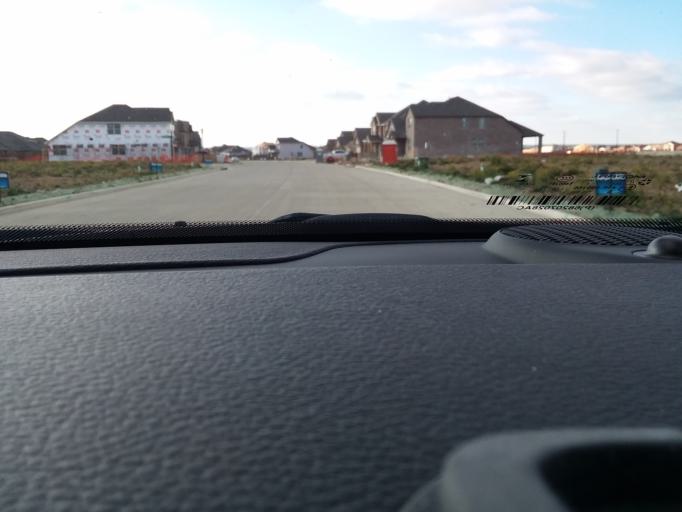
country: US
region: Texas
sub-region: Collin County
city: Prosper
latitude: 33.2653
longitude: -96.8842
